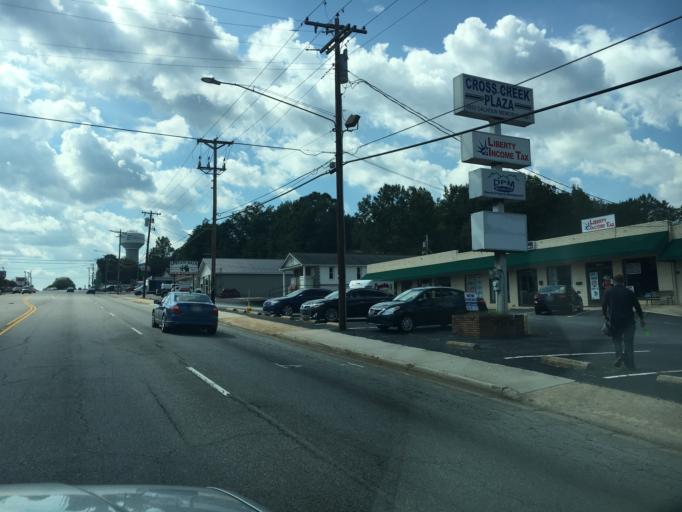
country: US
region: South Carolina
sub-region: Pickens County
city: Easley
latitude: 34.8203
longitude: -82.5938
